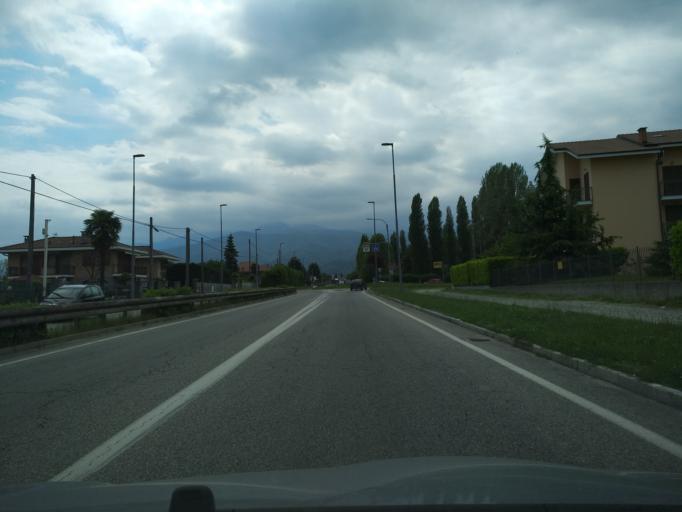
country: IT
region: Piedmont
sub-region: Provincia di Torino
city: Bricherasio
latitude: 44.8191
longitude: 7.3047
